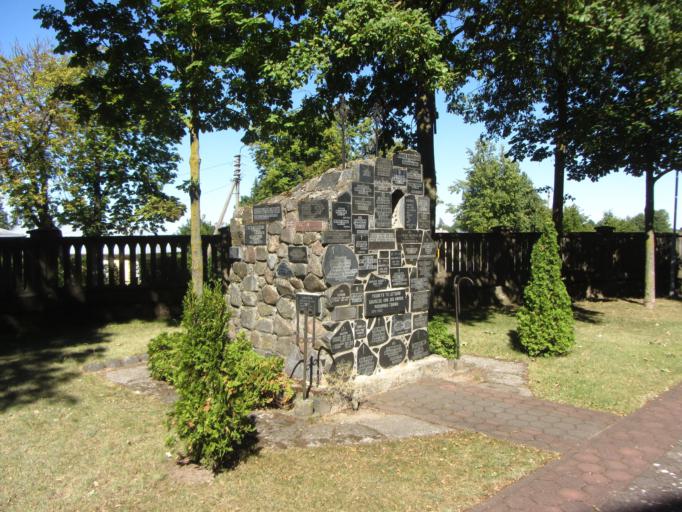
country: LT
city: Kupiskis
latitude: 55.8423
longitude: 24.9759
